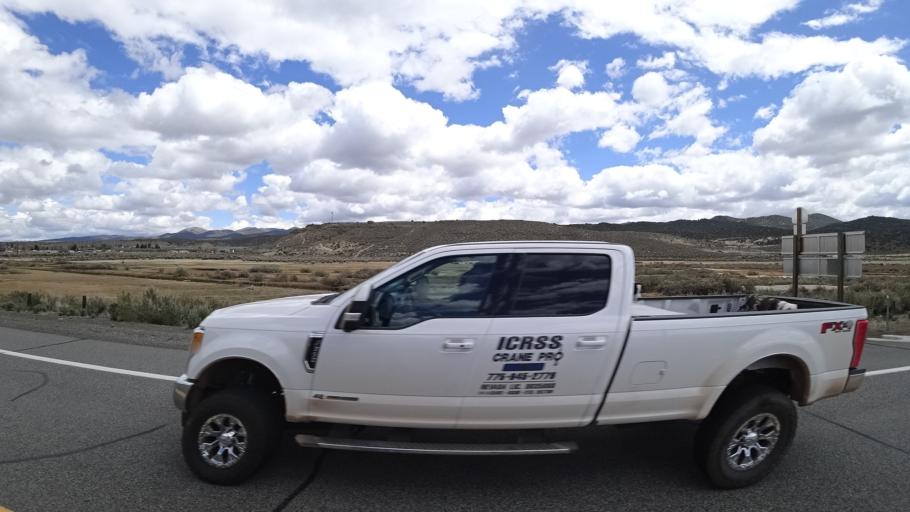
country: US
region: California
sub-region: Mono County
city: Bridgeport
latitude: 38.2538
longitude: -119.2226
